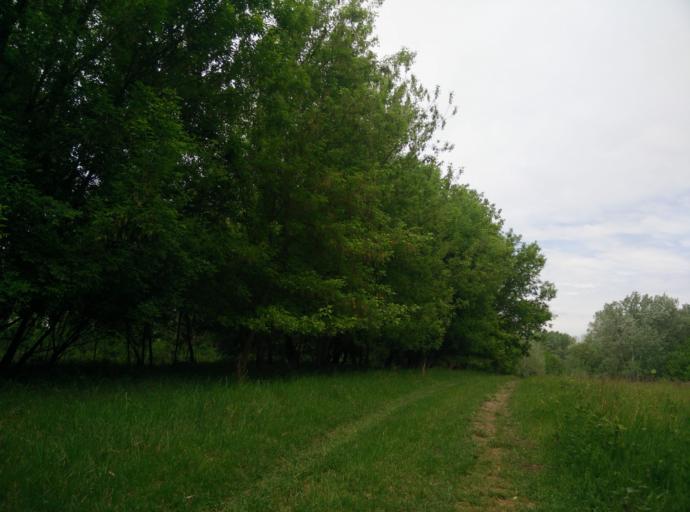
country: HU
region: Pest
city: Fot
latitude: 47.6030
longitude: 19.1559
